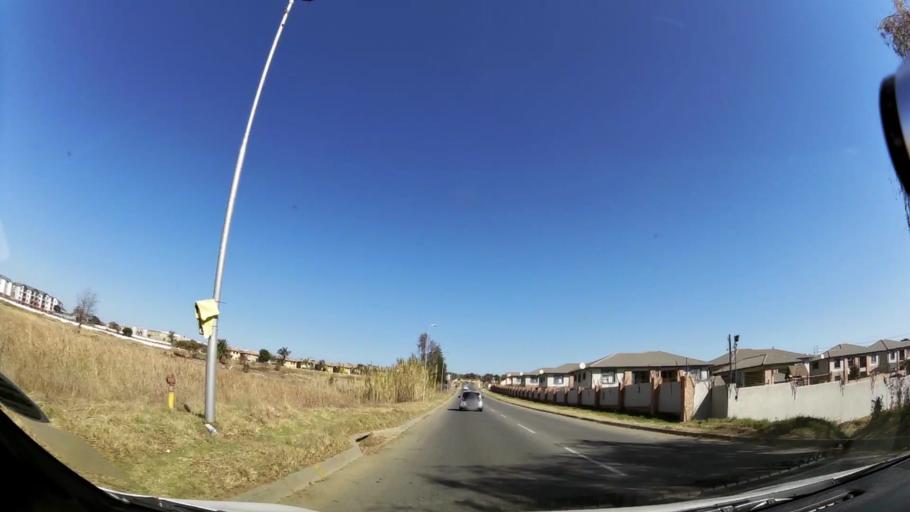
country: ZA
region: Gauteng
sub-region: City of Johannesburg Metropolitan Municipality
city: Midrand
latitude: -25.9692
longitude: 28.1070
